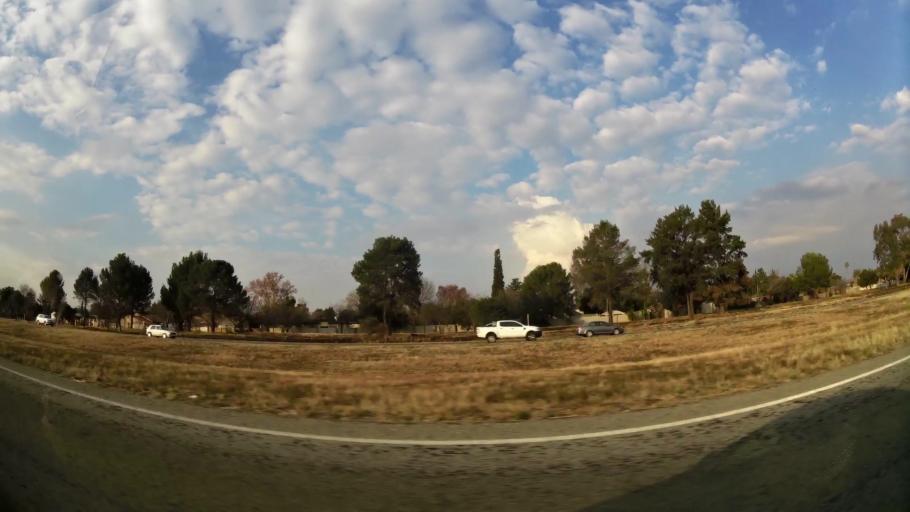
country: ZA
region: Gauteng
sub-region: Sedibeng District Municipality
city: Vanderbijlpark
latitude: -26.7345
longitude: 27.8220
